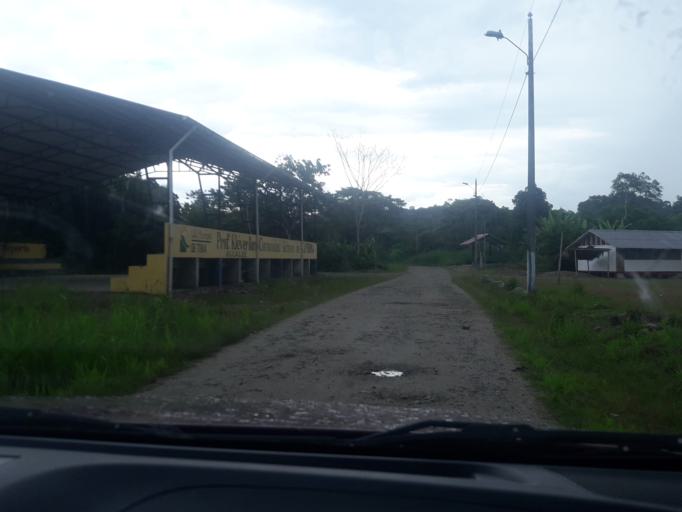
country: EC
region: Napo
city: Tena
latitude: -1.0988
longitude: -77.6831
